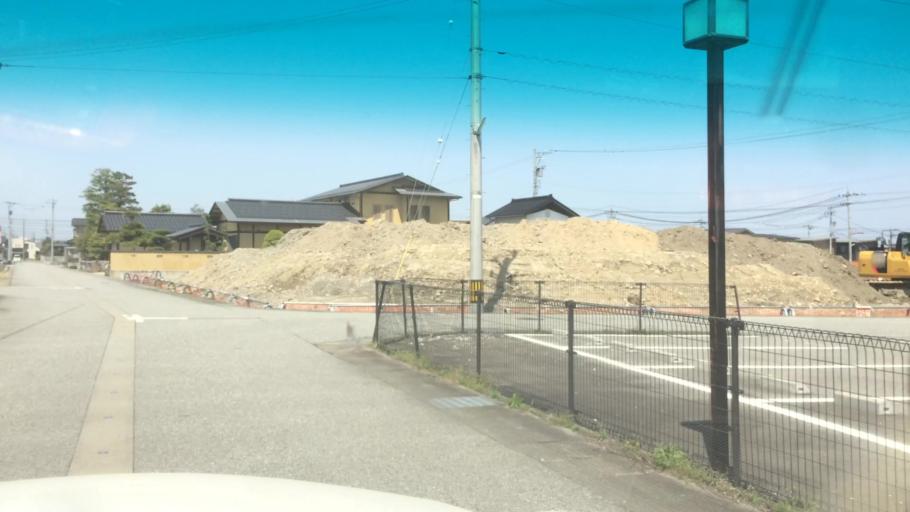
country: JP
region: Toyama
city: Toyama-shi
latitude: 36.6771
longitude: 137.2483
